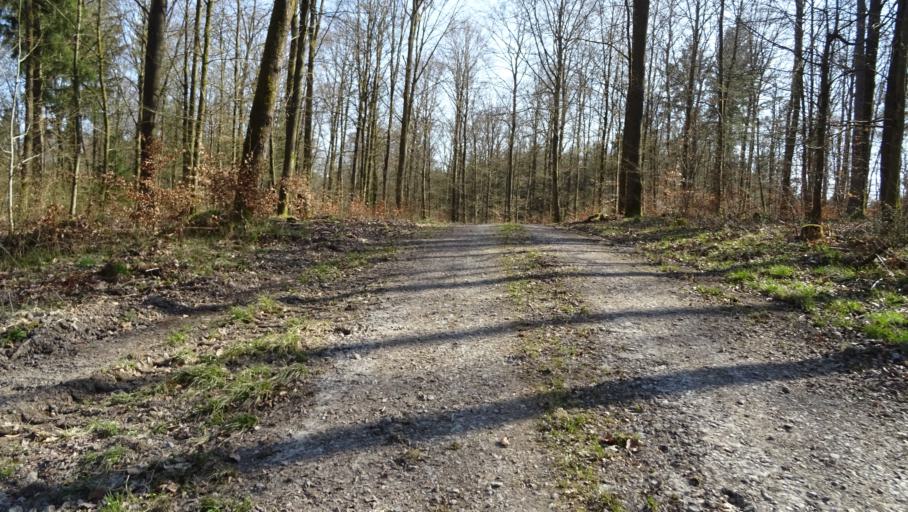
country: DE
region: Baden-Wuerttemberg
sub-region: Regierungsbezirk Stuttgart
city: Roigheim
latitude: 49.3938
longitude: 9.3379
